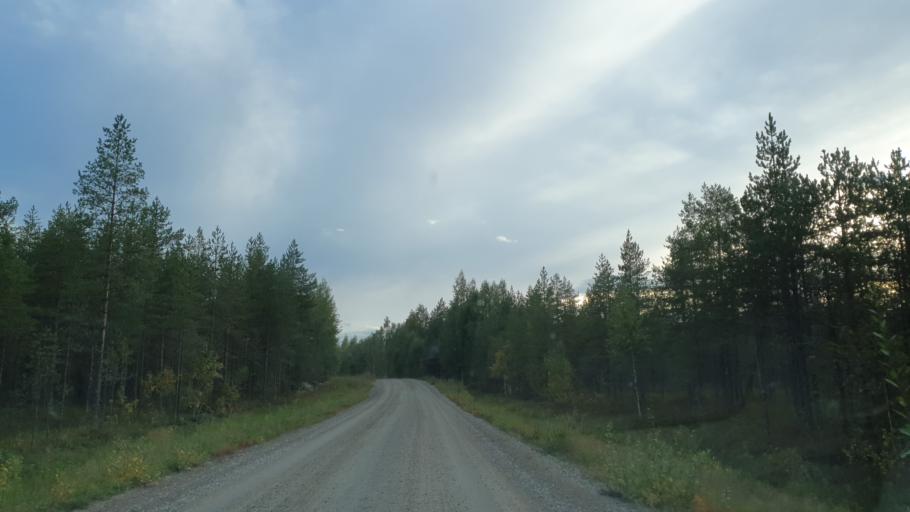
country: FI
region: Kainuu
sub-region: Kehys-Kainuu
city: Kuhmo
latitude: 64.3812
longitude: 29.5521
